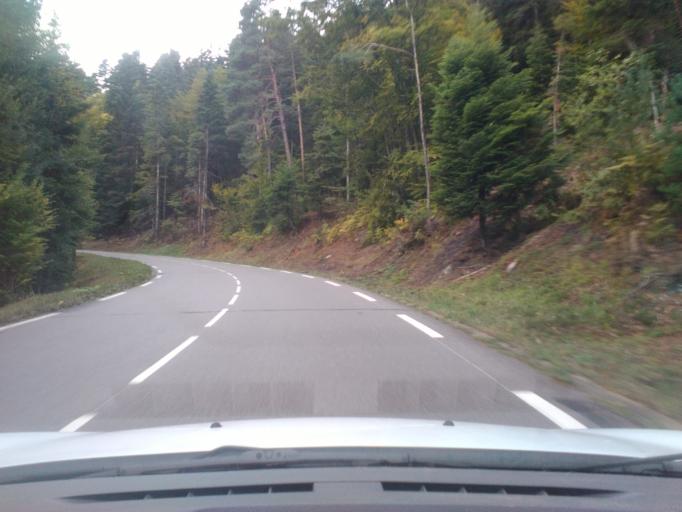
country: FR
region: Lorraine
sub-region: Departement des Vosges
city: Taintrux
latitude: 48.2714
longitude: 6.8824
